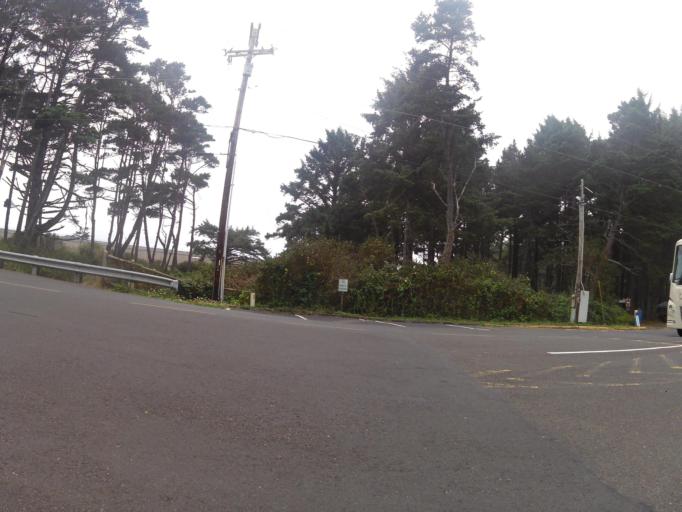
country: US
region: Oregon
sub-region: Lincoln County
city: Depoe Bay
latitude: 44.7285
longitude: -124.0553
